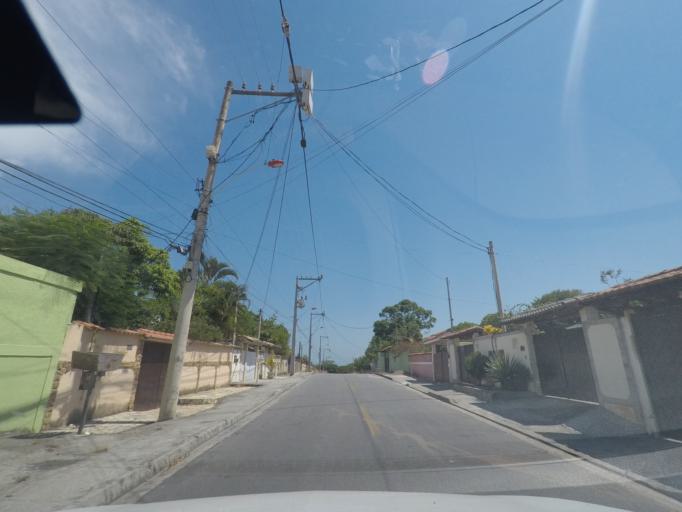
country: BR
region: Rio de Janeiro
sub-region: Marica
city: Marica
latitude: -22.9656
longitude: -42.9594
